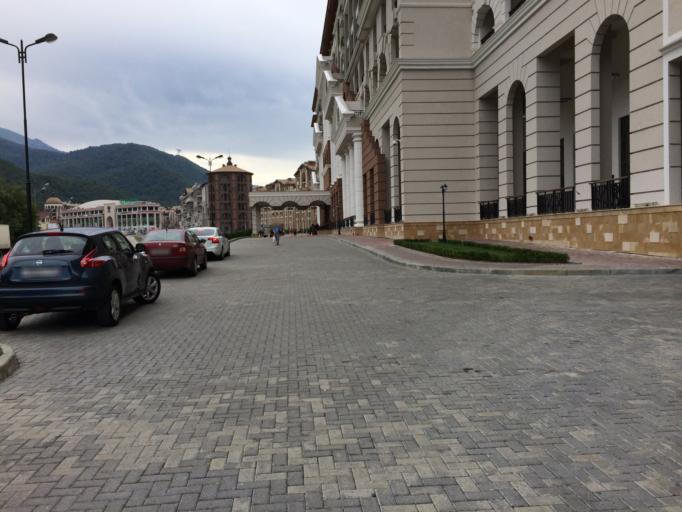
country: RU
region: Krasnodarskiy
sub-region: Sochi City
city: Krasnaya Polyana
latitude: 43.6843
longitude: 40.2556
